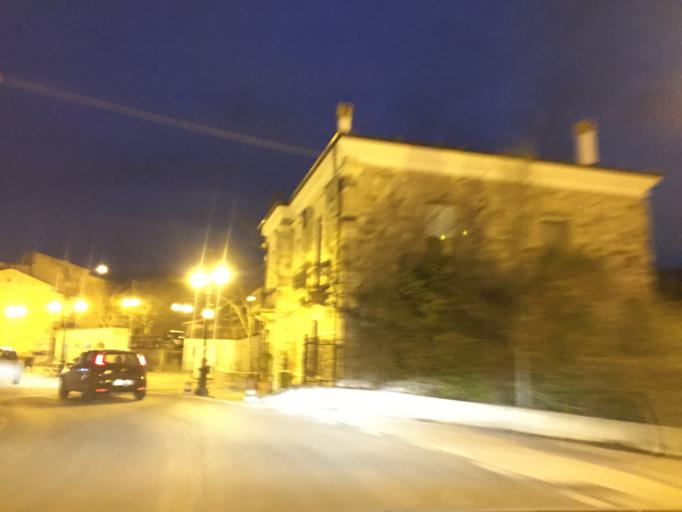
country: IT
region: Apulia
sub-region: Provincia di Foggia
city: Volturara Appula
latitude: 41.4966
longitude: 15.0542
